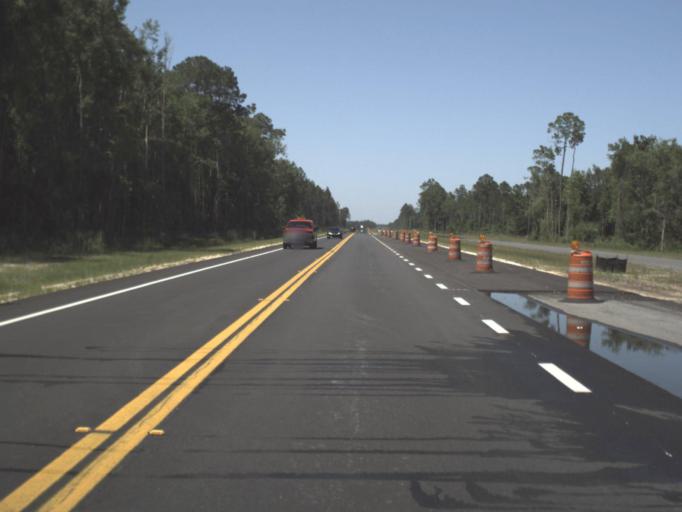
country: US
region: Florida
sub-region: Duval County
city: Baldwin
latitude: 30.3492
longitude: -81.9521
